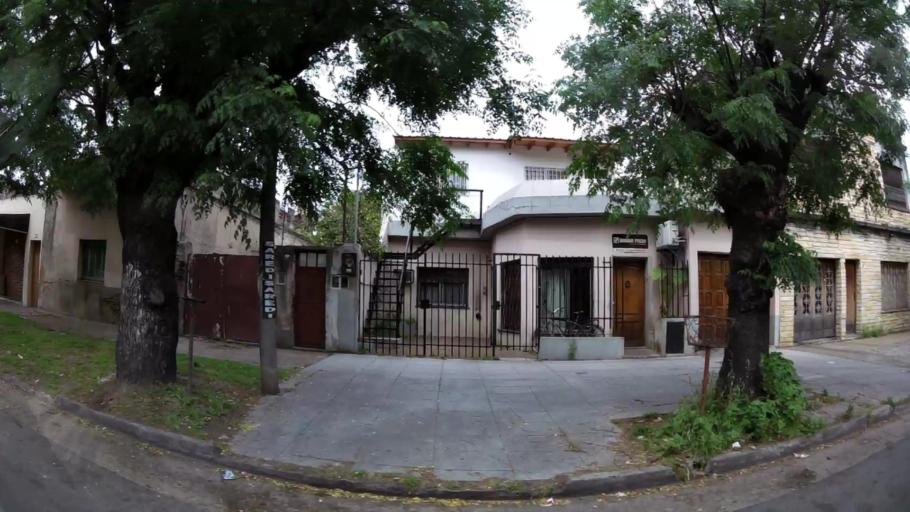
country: AR
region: Buenos Aires F.D.
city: Villa Lugano
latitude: -34.7046
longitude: -58.5058
